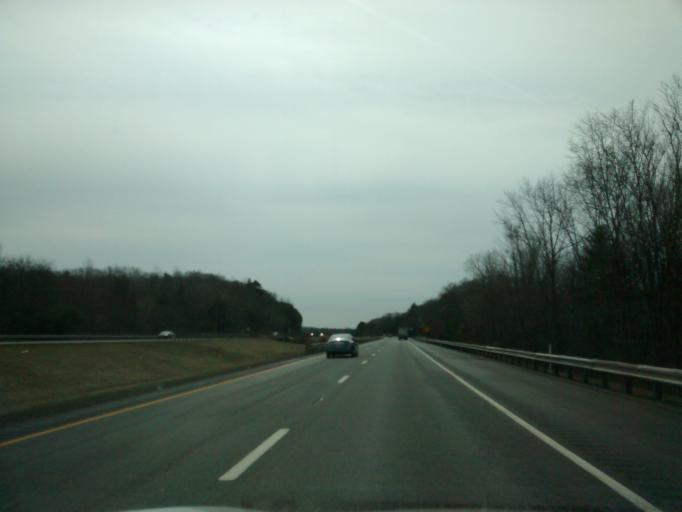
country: US
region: Massachusetts
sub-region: Worcester County
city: Oxford
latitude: 42.1327
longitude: -71.8571
